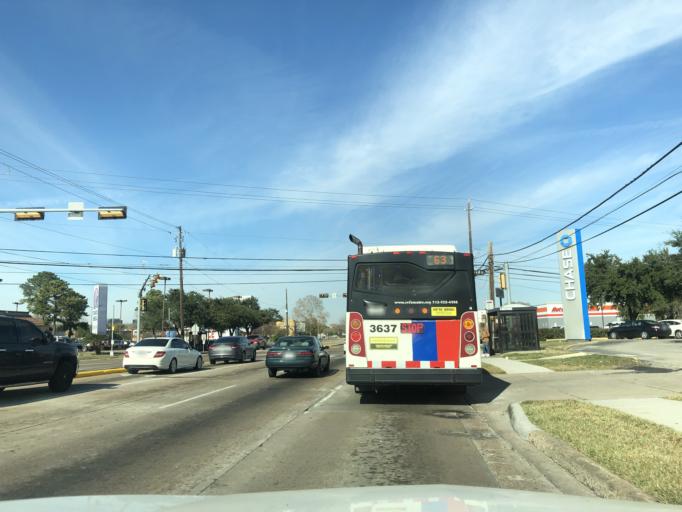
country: US
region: Texas
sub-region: Harris County
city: Bellaire
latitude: 29.6863
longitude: -95.5087
